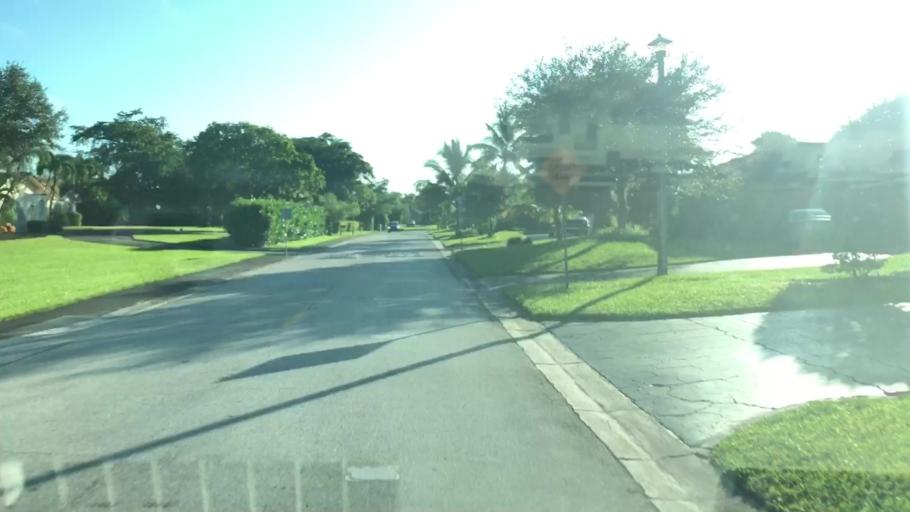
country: US
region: Florida
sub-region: Broward County
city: Coral Springs
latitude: 26.2777
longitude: -80.2614
